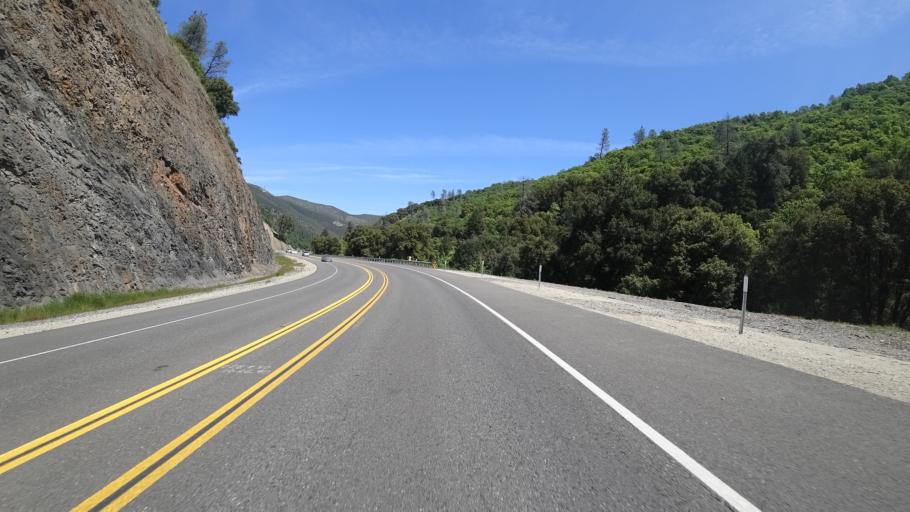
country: US
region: California
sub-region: Trinity County
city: Lewiston
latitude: 40.6689
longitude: -122.6861
